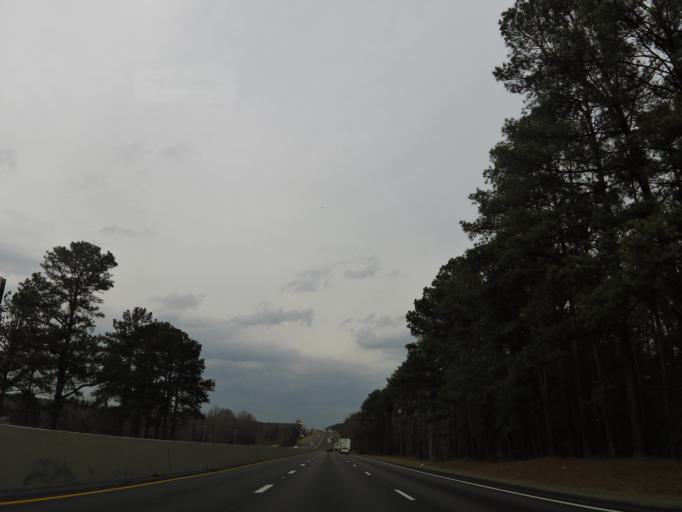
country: US
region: South Carolina
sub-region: Lexington County
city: Gaston
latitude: 33.8503
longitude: -81.0268
